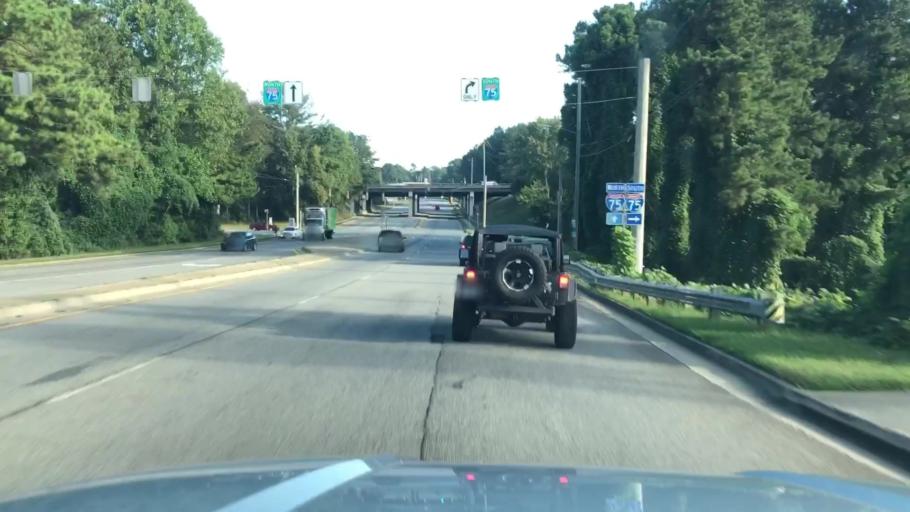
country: US
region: Georgia
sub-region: Cobb County
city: Acworth
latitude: 34.0786
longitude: -84.6764
